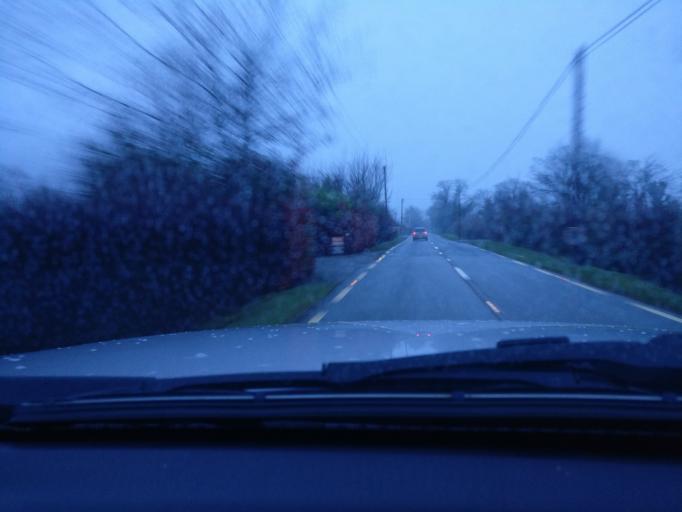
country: IE
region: Leinster
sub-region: An Mhi
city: Athboy
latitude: 53.6413
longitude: -6.8386
